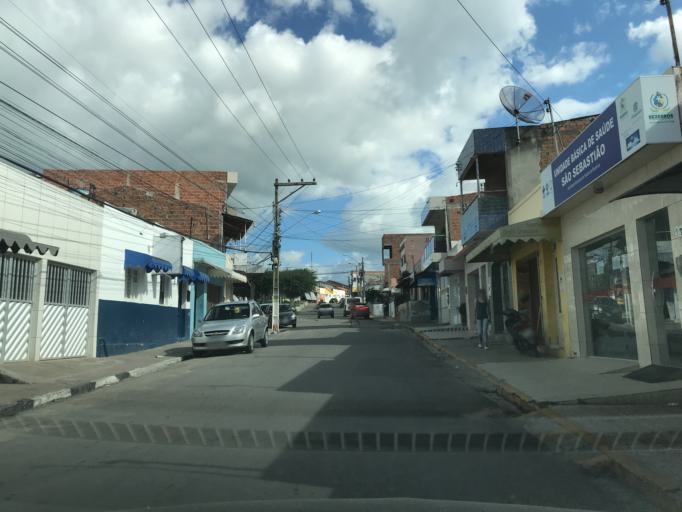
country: BR
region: Pernambuco
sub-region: Bezerros
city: Bezerros
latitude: -8.2369
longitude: -35.7529
